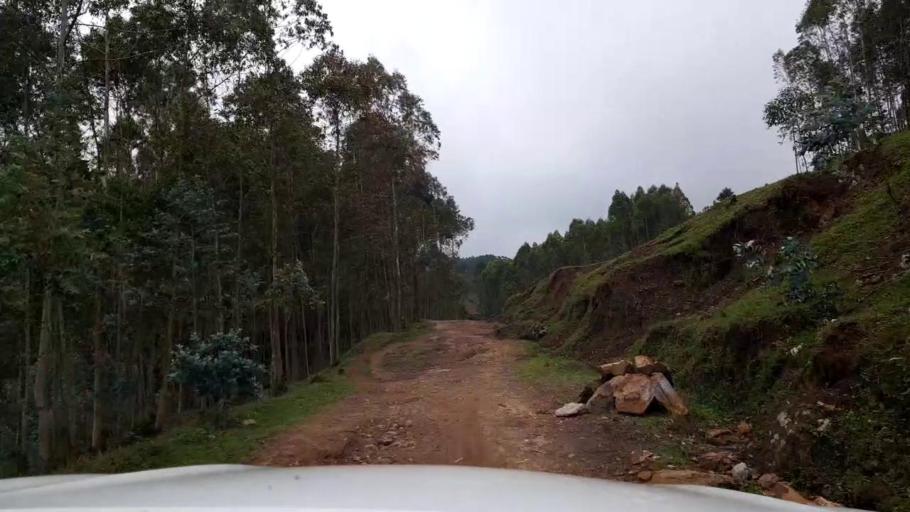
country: RW
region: Northern Province
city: Musanze
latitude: -1.6076
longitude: 29.7673
